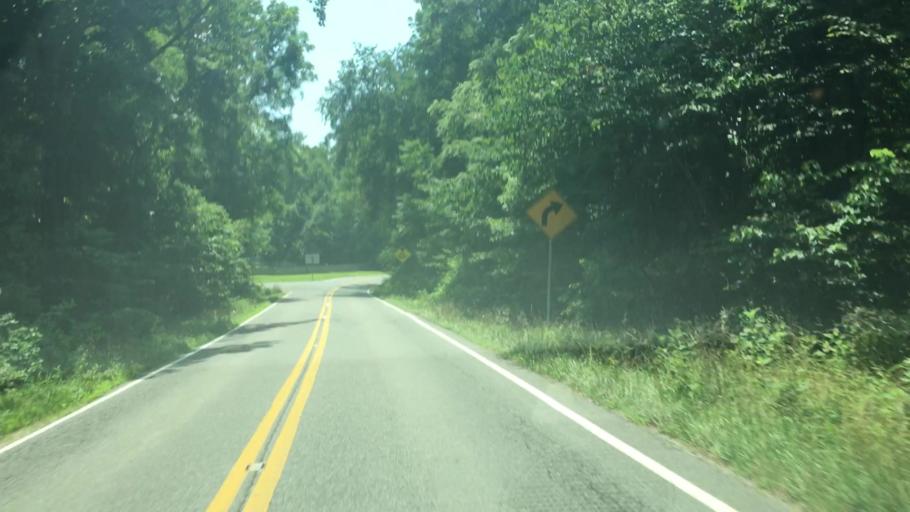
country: US
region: Virginia
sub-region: King George County
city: King George
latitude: 38.3307
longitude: -77.1446
